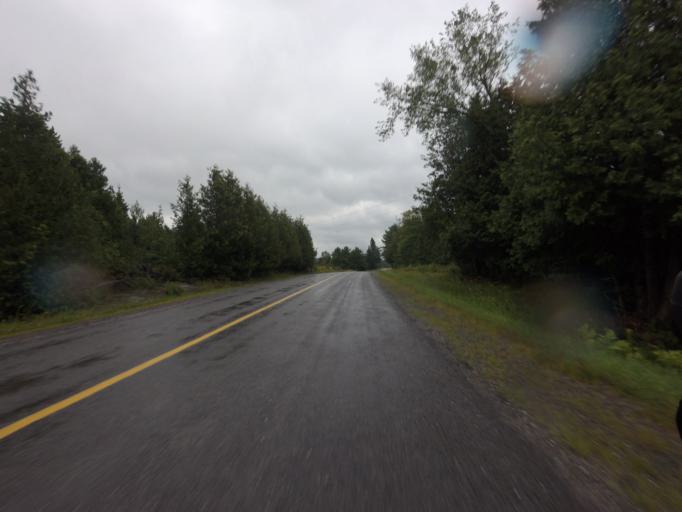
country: CA
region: Ontario
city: Renfrew
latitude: 45.0679
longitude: -76.6385
